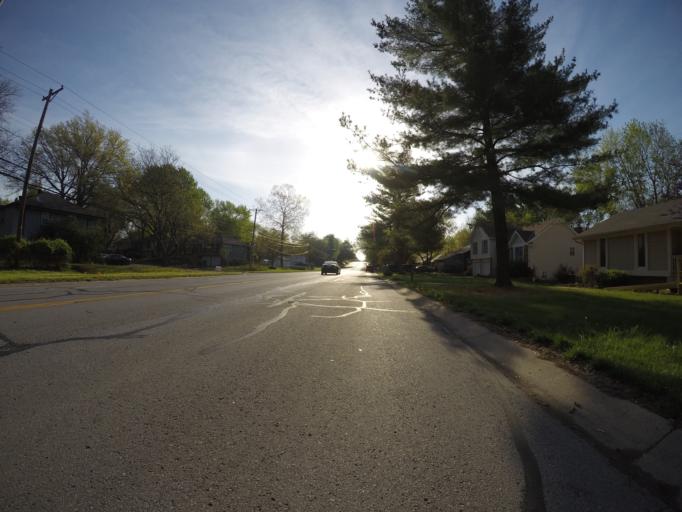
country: US
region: Missouri
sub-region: Jackson County
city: Lees Summit
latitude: 38.9117
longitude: -94.4113
